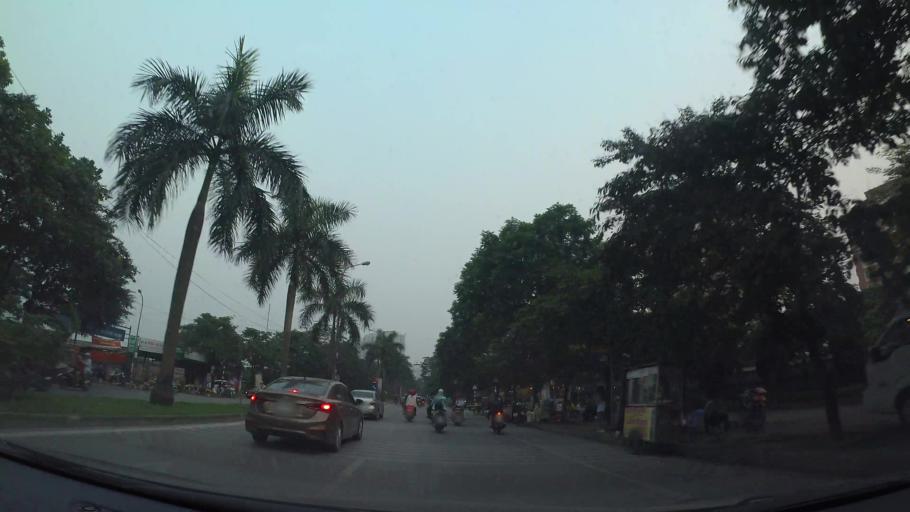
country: VN
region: Ha Noi
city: Ha Dong
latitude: 20.9738
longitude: 105.7899
